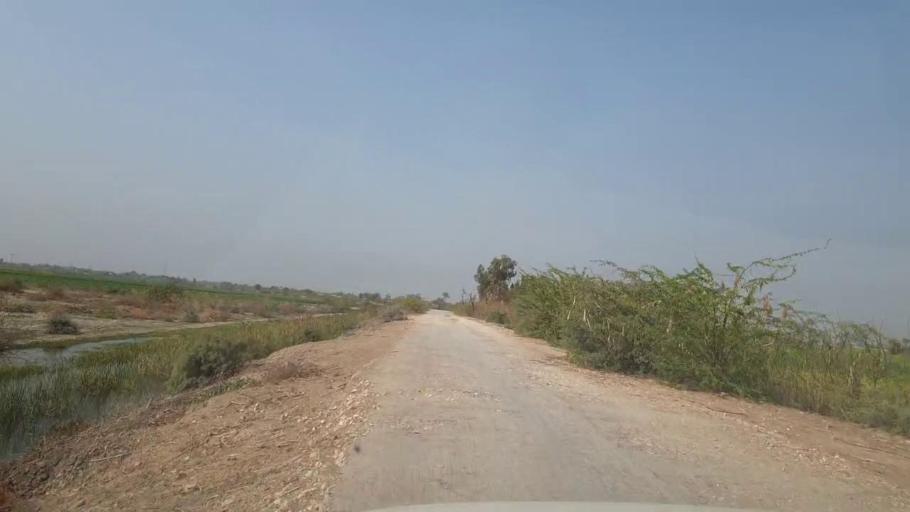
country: PK
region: Sindh
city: Mirpur Khas
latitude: 25.6966
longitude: 69.1465
